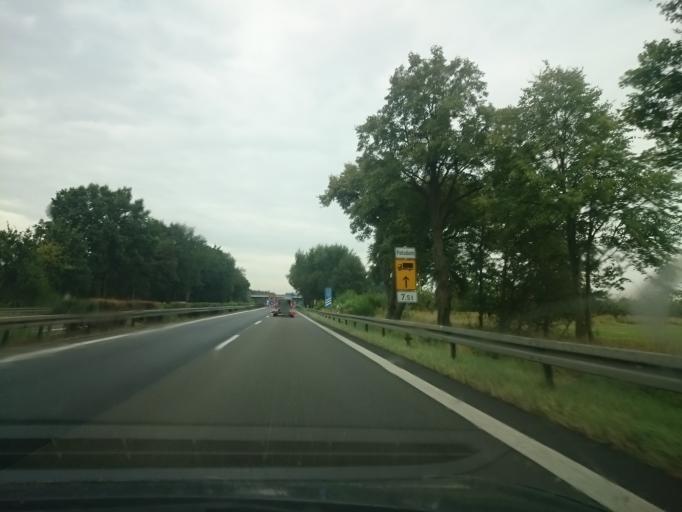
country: DE
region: Brandenburg
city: Werder
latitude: 52.4382
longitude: 12.9302
